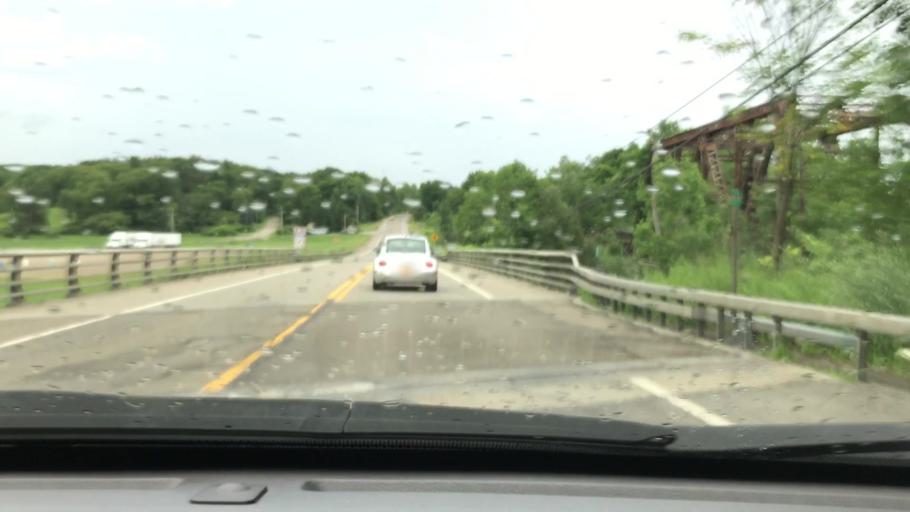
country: US
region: New York
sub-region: Cattaraugus County
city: Salamanca
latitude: 42.1850
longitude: -78.6814
